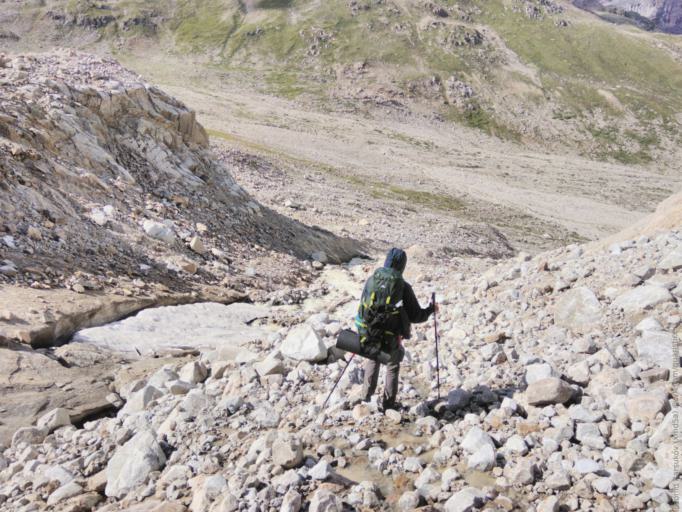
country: RU
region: Kabardino-Balkariya
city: Terskol
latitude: 43.2610
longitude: 42.4347
